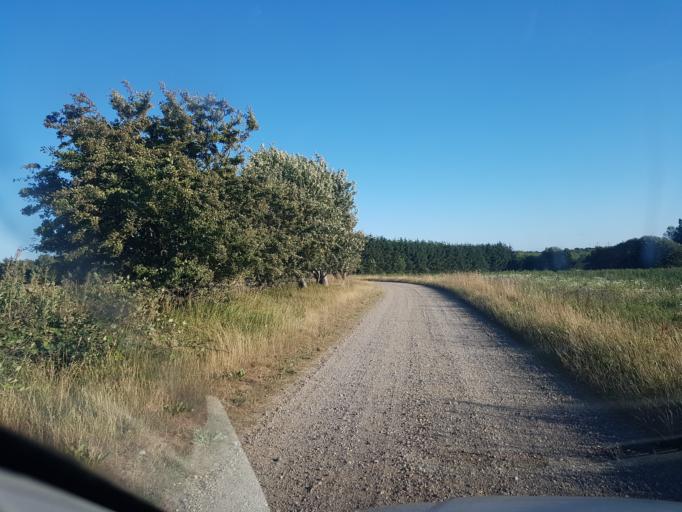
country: DK
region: South Denmark
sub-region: Esbjerg Kommune
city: Esbjerg
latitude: 55.4881
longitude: 8.5073
